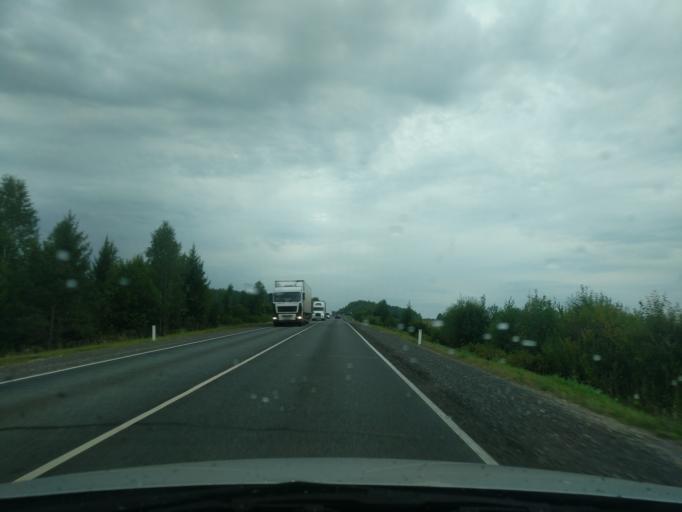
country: RU
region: Kirov
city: Orlov
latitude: 58.6746
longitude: 49.0662
